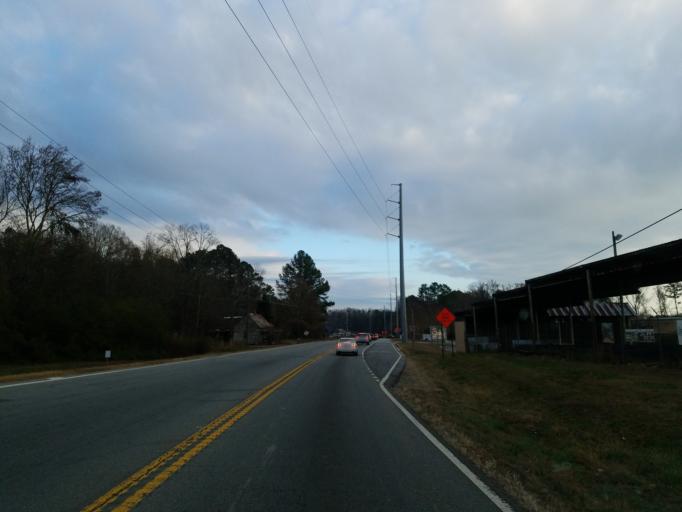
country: US
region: Georgia
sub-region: Forsyth County
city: Cumming
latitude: 34.2695
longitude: -84.0948
